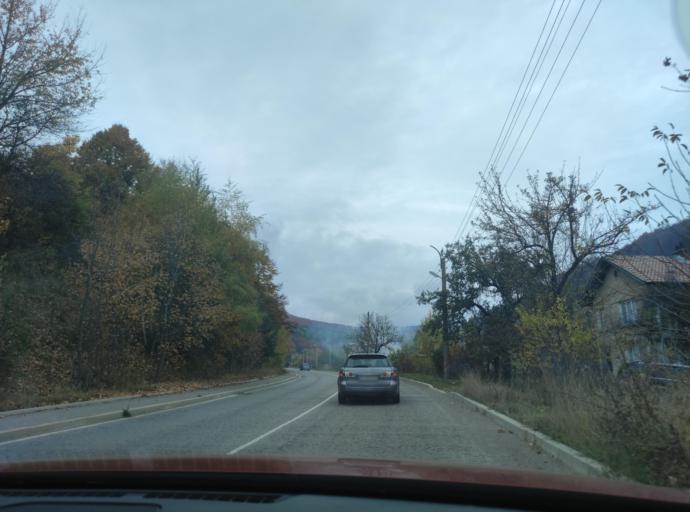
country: BG
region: Sofiya
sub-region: Obshtina Godech
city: Godech
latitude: 43.0854
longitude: 23.1024
